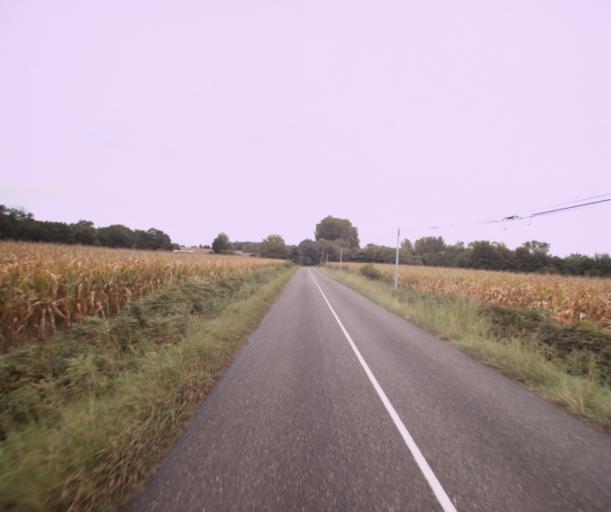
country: FR
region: Midi-Pyrenees
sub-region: Departement du Gers
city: Cazaubon
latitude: 43.8664
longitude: -0.0787
